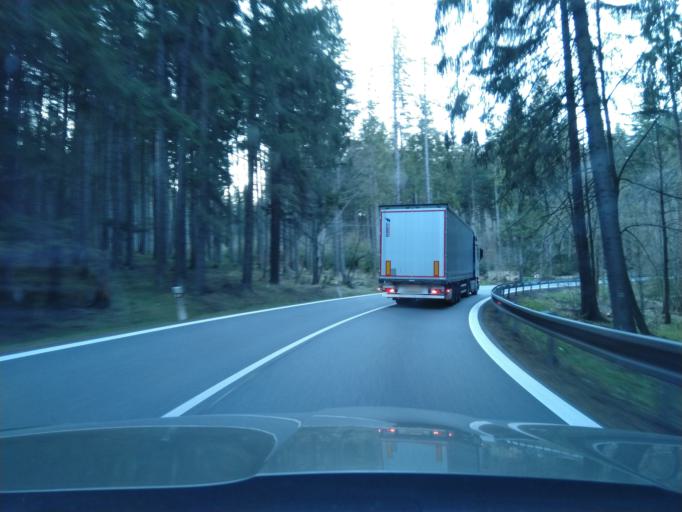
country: CZ
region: Jihocesky
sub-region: Okres Prachatice
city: Vimperk
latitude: 49.0392
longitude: 13.7633
